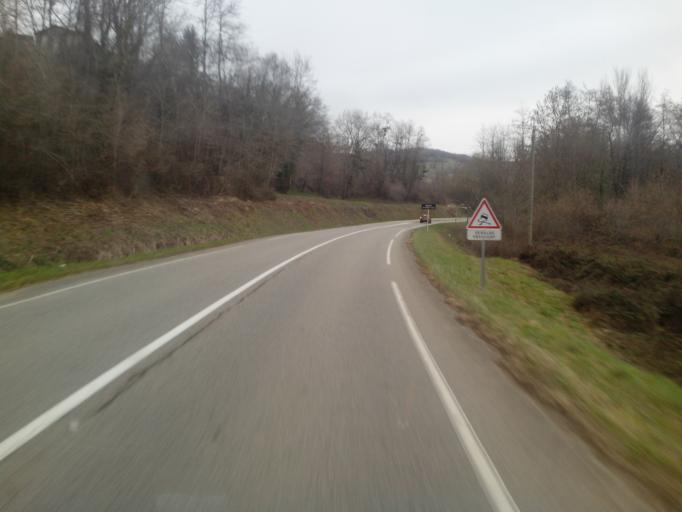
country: FR
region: Midi-Pyrenees
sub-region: Departement de l'Ariege
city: Montjoie-en-Couserans
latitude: 43.0142
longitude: 1.3689
